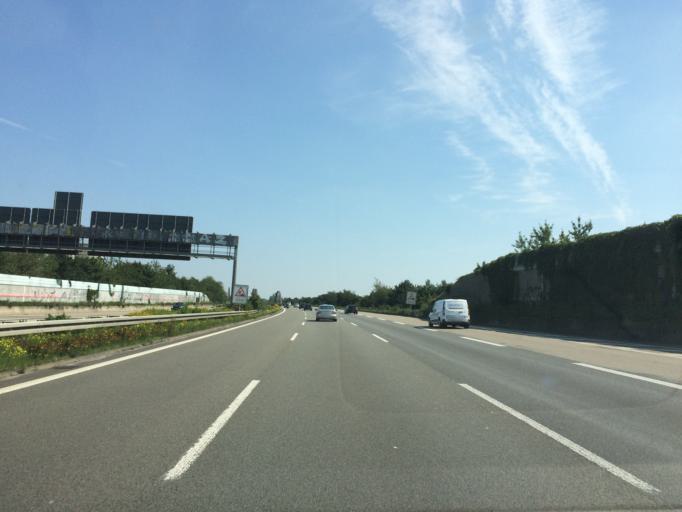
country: DE
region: North Rhine-Westphalia
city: Waltrop
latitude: 51.5834
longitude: 7.4006
